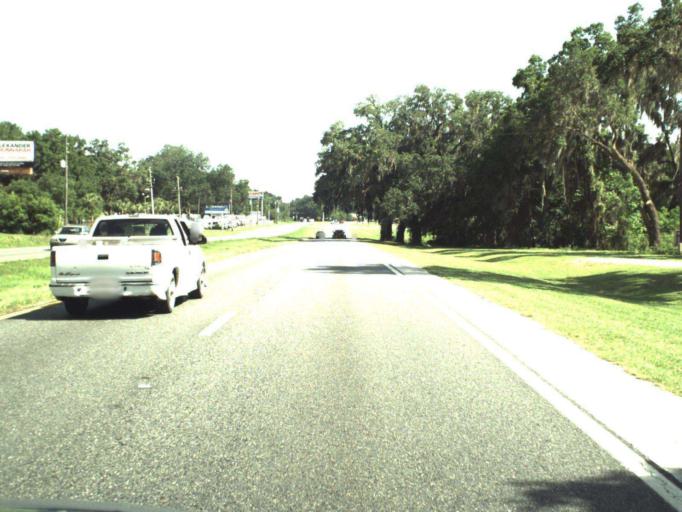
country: US
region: Florida
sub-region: Marion County
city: Belleview
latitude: 29.1121
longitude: -82.0948
